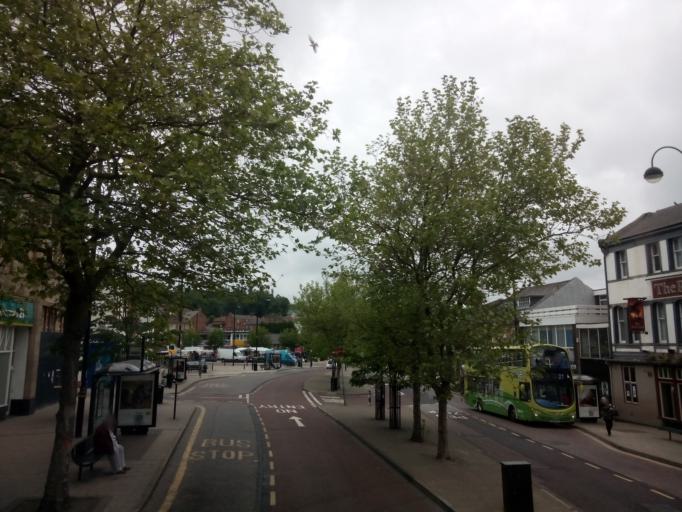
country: GB
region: England
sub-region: County Durham
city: Chester-le-Street
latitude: 54.8577
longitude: -1.5741
